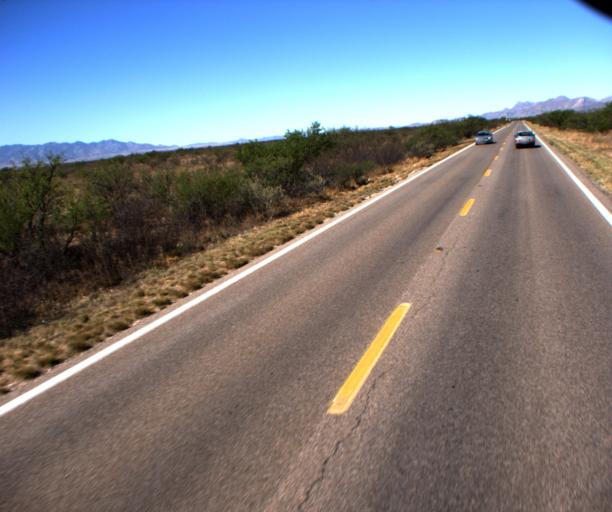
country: US
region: Arizona
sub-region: Cochise County
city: Huachuca City
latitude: 31.7099
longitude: -110.2732
